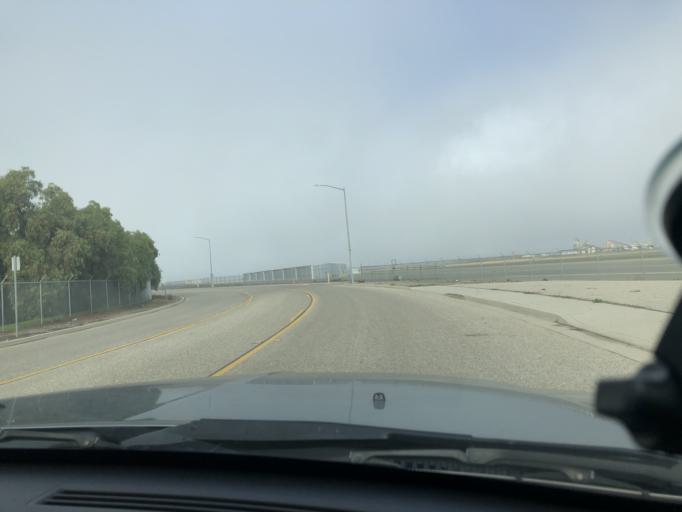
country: US
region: California
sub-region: Monterey County
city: King City
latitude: 36.2248
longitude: -121.1183
